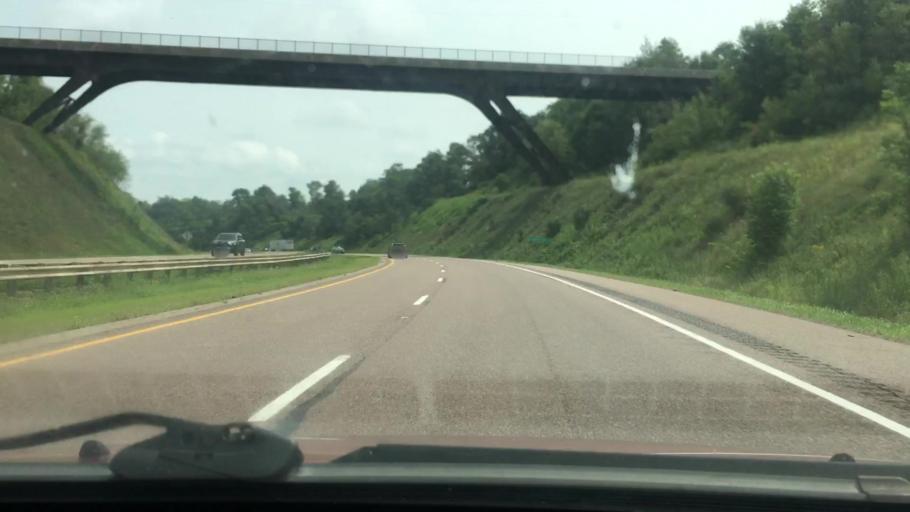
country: US
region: West Virginia
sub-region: Preston County
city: Terra Alta
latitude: 39.6533
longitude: -79.4404
